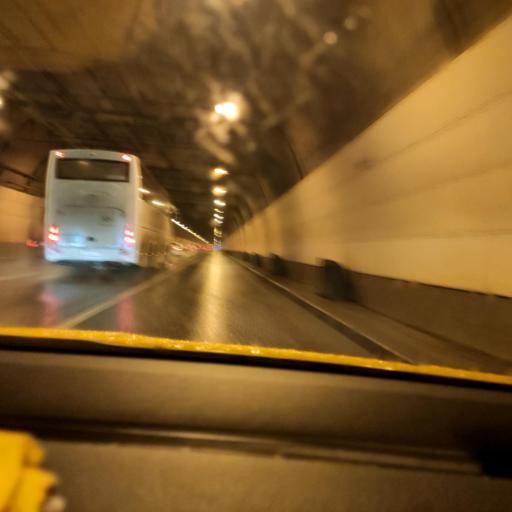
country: RU
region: Moscow
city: Rublevo
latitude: 55.7833
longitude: 37.3924
